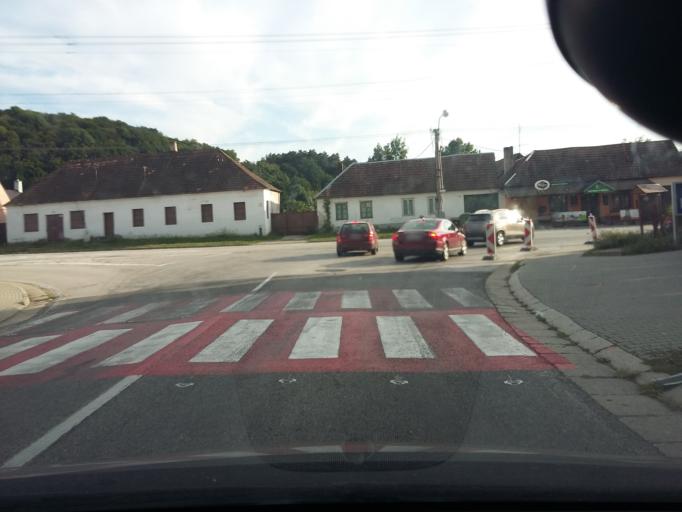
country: SK
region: Bratislavsky
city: Svaty Jur
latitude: 48.3678
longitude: 17.1439
